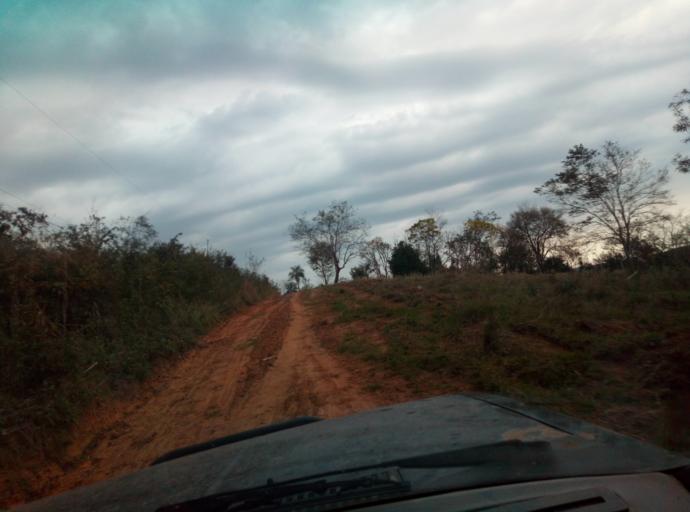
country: PY
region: Caaguazu
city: Doctor Cecilio Baez
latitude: -25.1445
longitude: -56.2243
